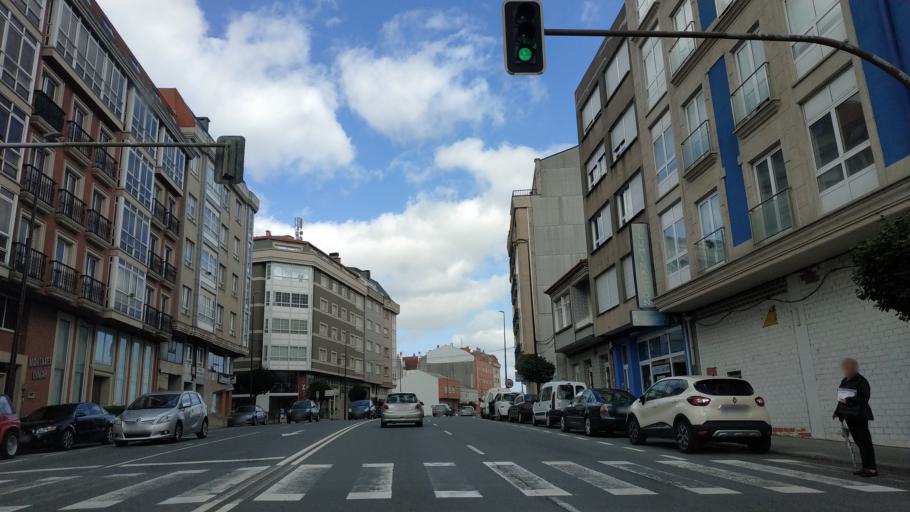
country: ES
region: Galicia
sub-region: Provincia da Coruna
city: Carballo
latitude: 43.2197
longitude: -8.6869
